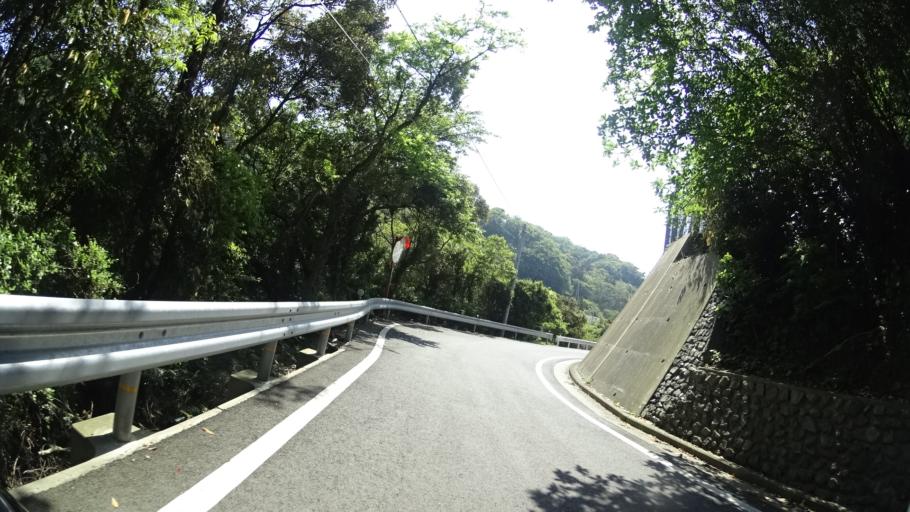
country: JP
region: Oita
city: Tsukumiura
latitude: 33.3599
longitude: 132.0379
